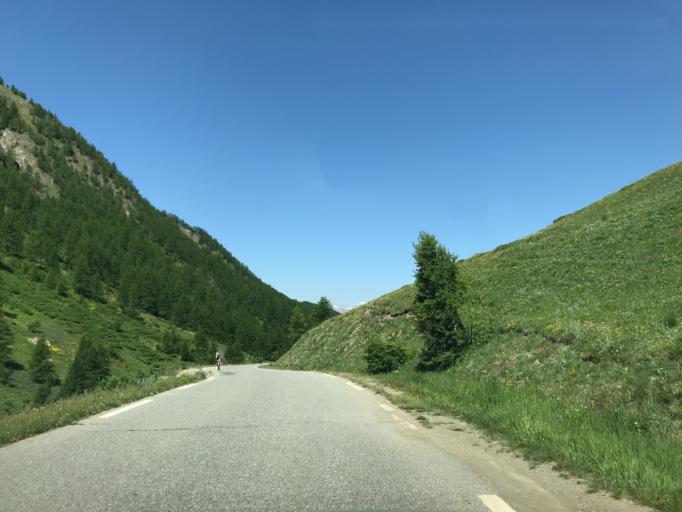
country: IT
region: Piedmont
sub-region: Provincia di Cuneo
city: Pontechianale
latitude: 44.7070
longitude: 6.9279
